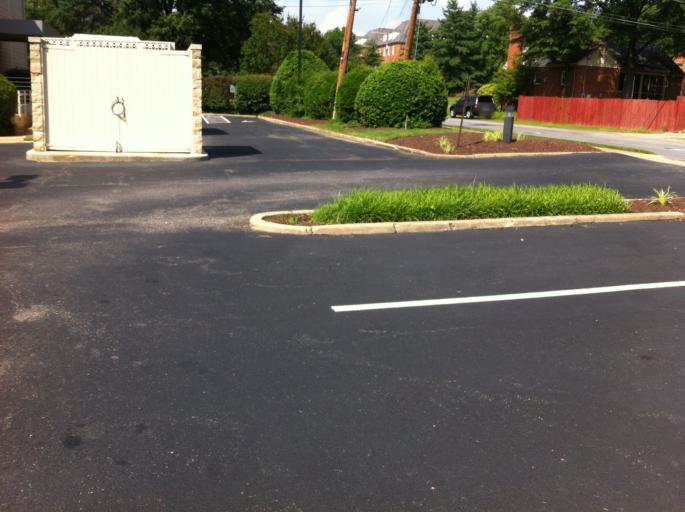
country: US
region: Virginia
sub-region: Henrico County
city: Dumbarton
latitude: 37.5776
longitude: -77.5015
